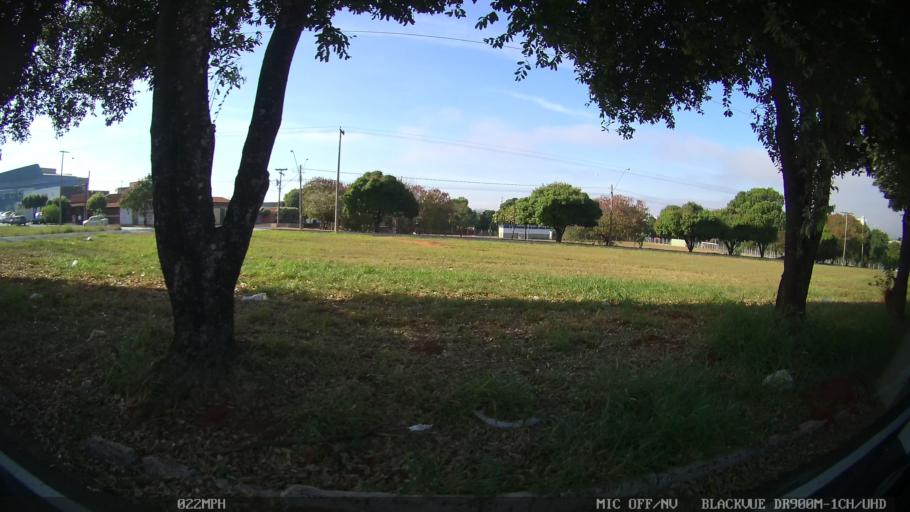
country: BR
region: Sao Paulo
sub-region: Sao Jose Do Rio Preto
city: Sao Jose do Rio Preto
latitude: -20.7874
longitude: -49.4109
